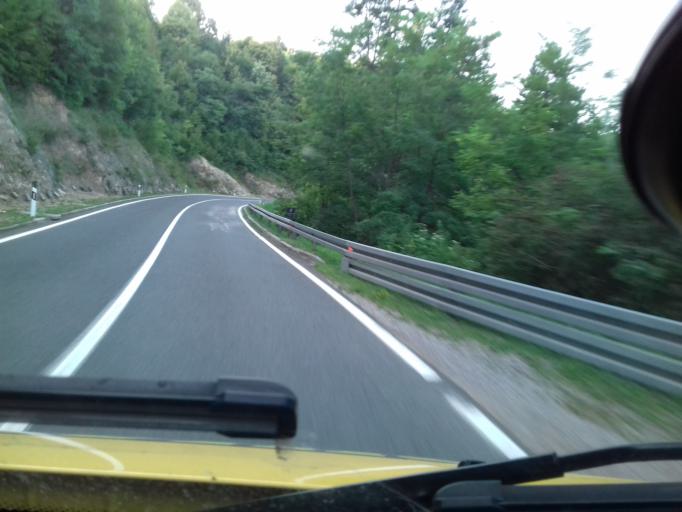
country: BA
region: Federation of Bosnia and Herzegovina
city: Ostrozac
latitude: 44.9011
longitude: 15.9307
